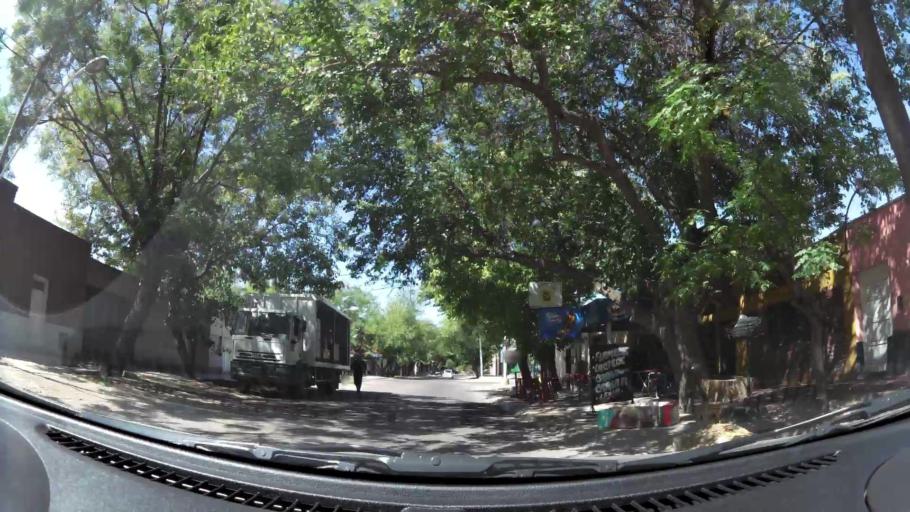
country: AR
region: Mendoza
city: Mendoza
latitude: -32.8852
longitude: -68.8150
